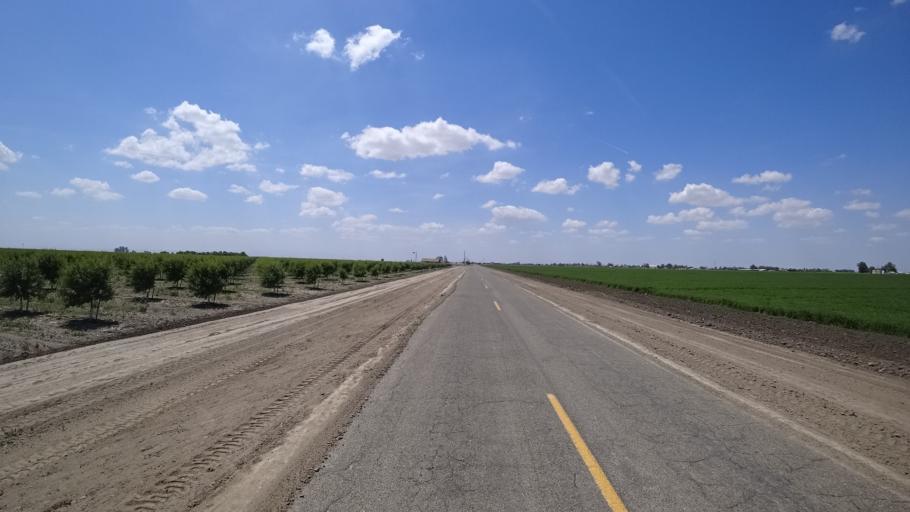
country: US
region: California
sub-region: Kings County
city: Stratford
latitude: 36.1822
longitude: -119.8045
